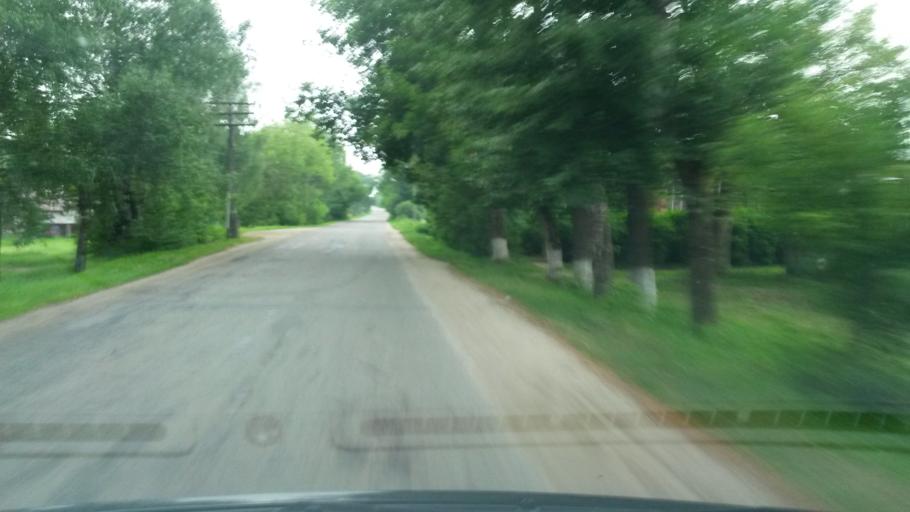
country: RU
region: Ivanovo
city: Pistsovo
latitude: 57.1784
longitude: 40.5291
